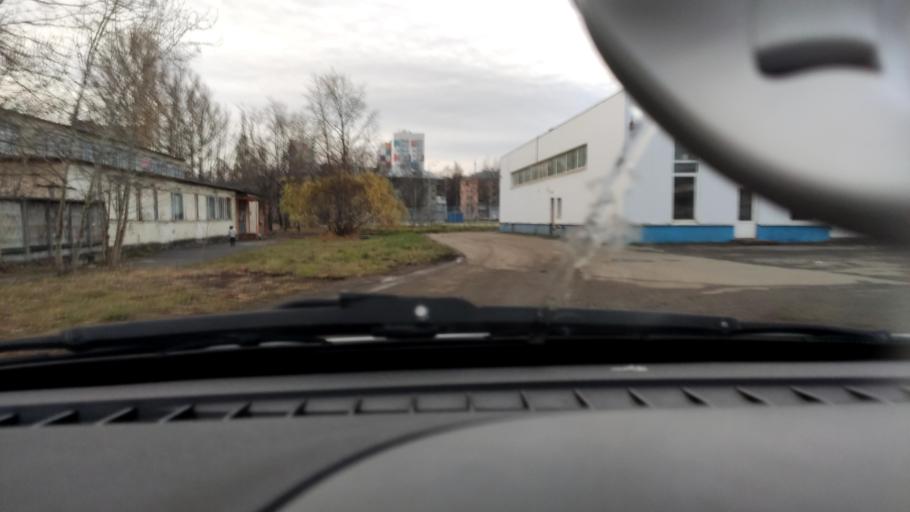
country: RU
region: Perm
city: Perm
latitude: 58.0070
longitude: 56.2928
